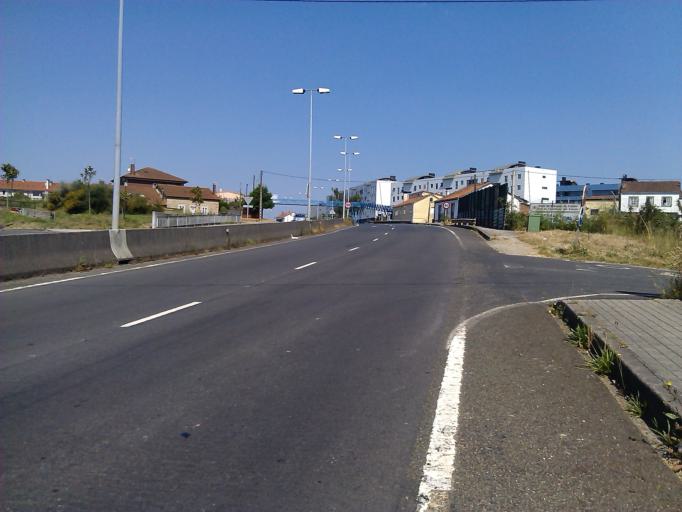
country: ES
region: Galicia
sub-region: Provincia da Coruna
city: Santiago de Compostela
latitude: 42.8572
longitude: -8.5330
